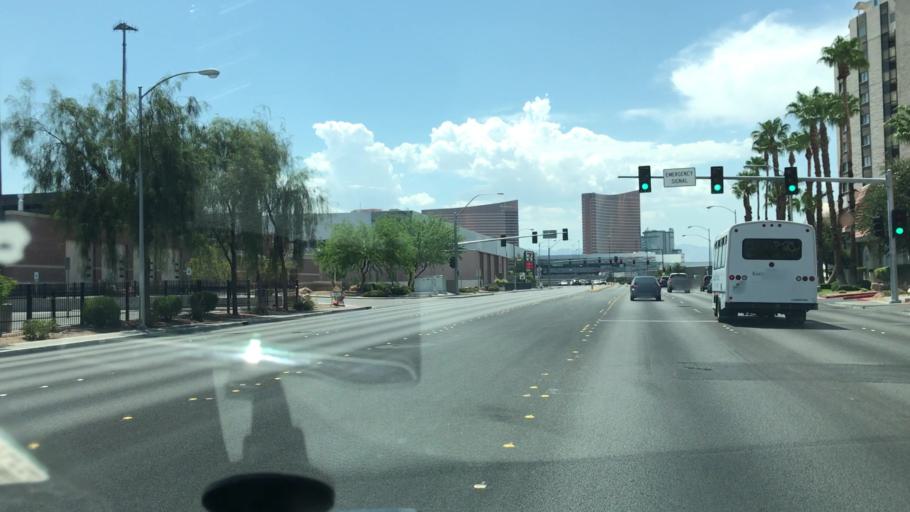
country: US
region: Nevada
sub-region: Clark County
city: Winchester
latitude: 36.1298
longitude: -115.1435
